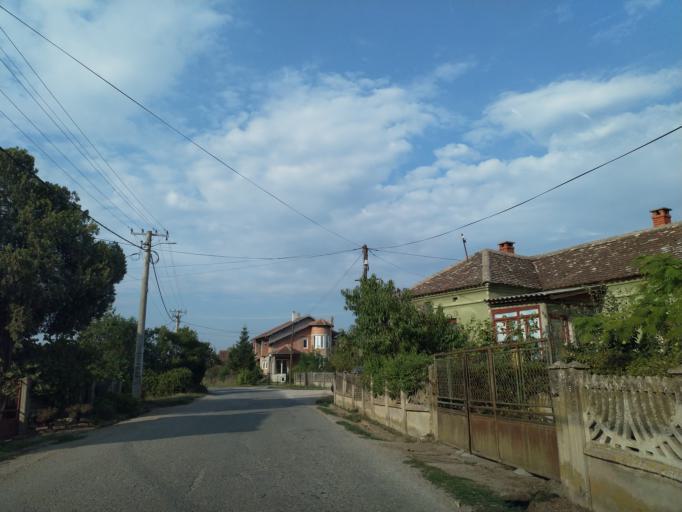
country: RS
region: Central Serbia
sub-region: Pomoravski Okrug
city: Paracin
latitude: 43.8432
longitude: 21.4801
